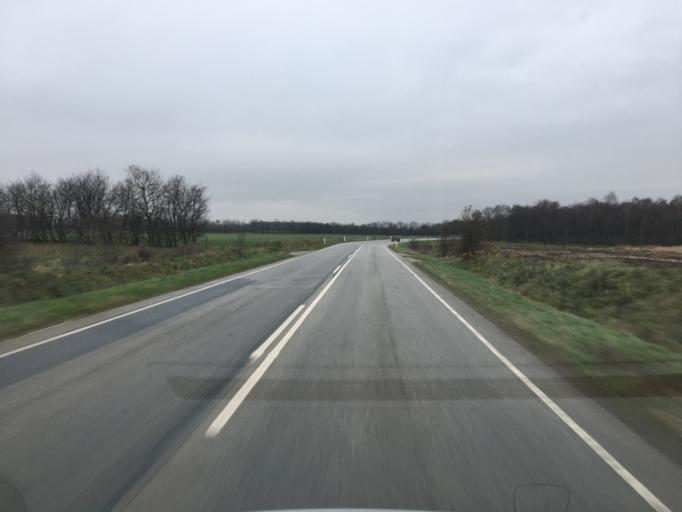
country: DK
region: South Denmark
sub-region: Aabenraa Kommune
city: Tinglev
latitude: 54.9989
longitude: 9.2376
